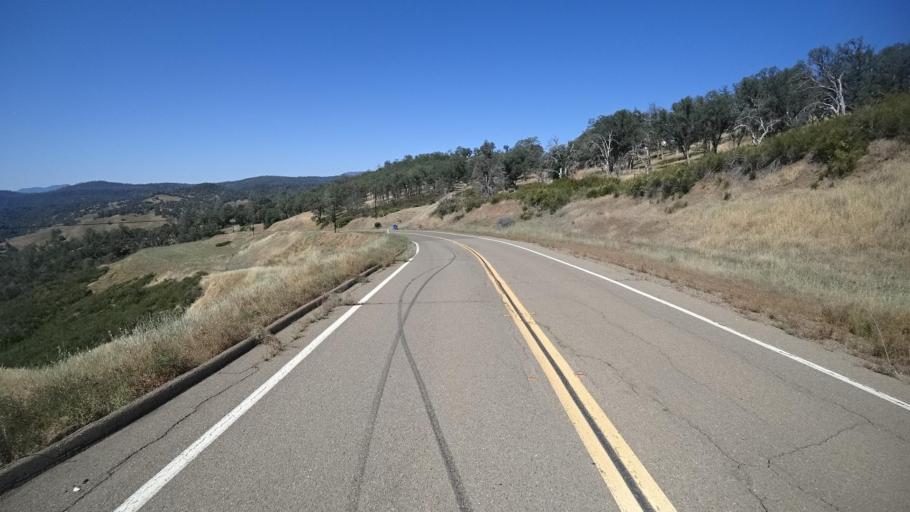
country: US
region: California
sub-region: Lake County
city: Hidden Valley Lake
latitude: 38.8829
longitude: -122.5221
